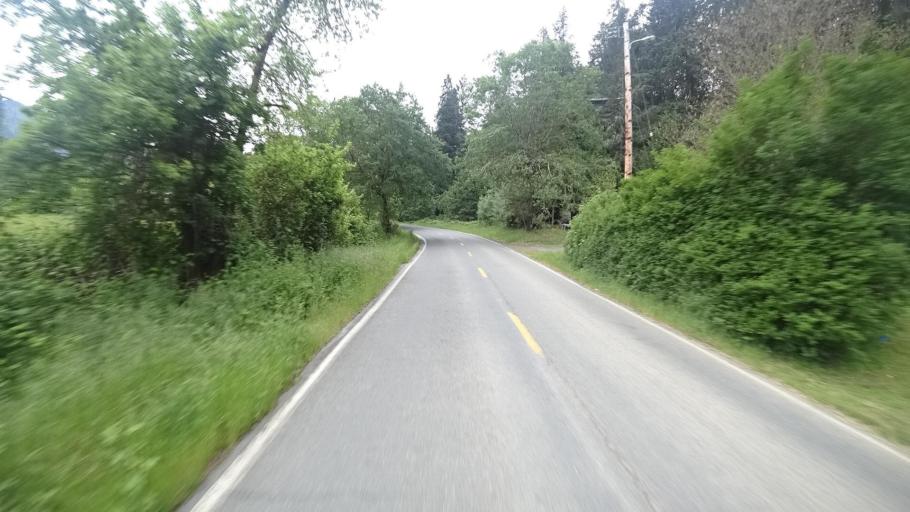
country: US
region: California
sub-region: Humboldt County
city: Willow Creek
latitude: 41.0877
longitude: -123.7112
